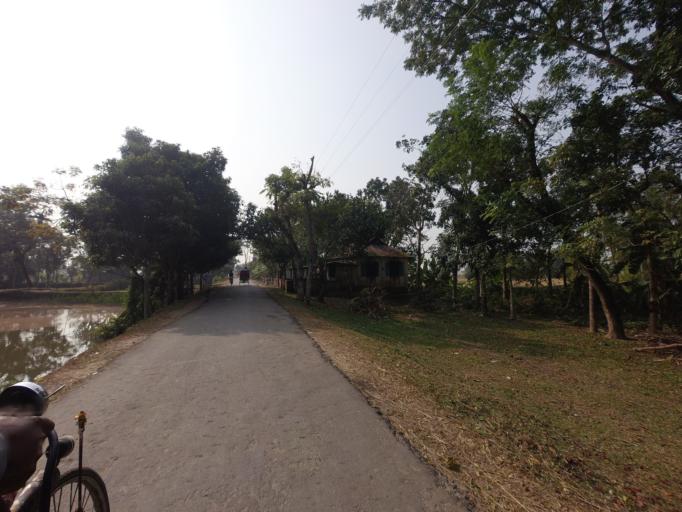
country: BD
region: Dhaka
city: Netrakona
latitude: 25.0593
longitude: 90.6922
